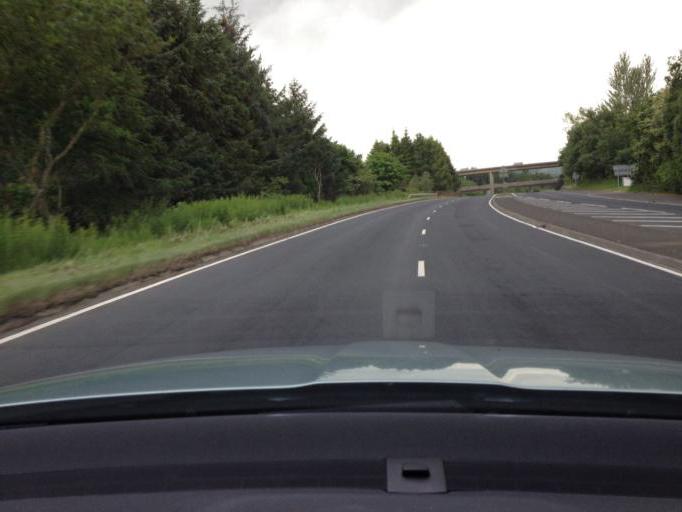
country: GB
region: Scotland
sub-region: Perth and Kinross
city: Perth
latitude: 56.3716
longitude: -3.4232
